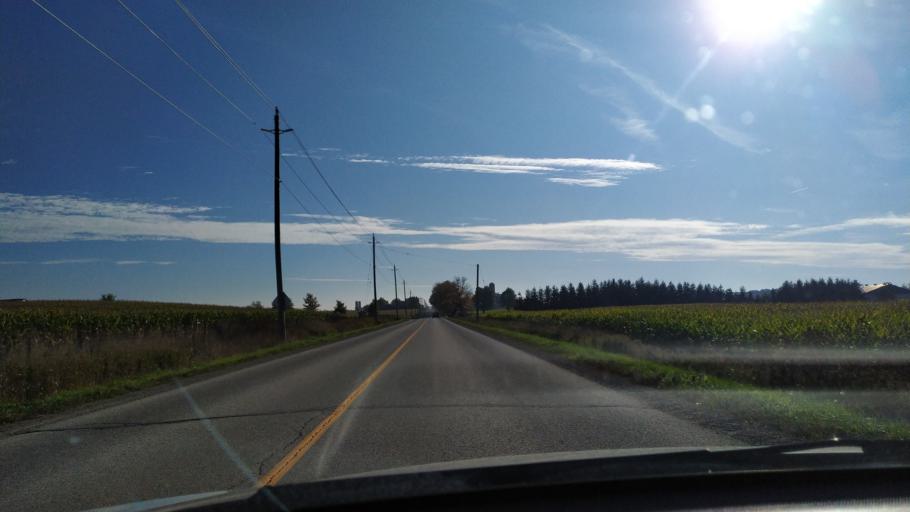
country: CA
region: Ontario
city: Waterloo
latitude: 43.4933
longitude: -80.7338
